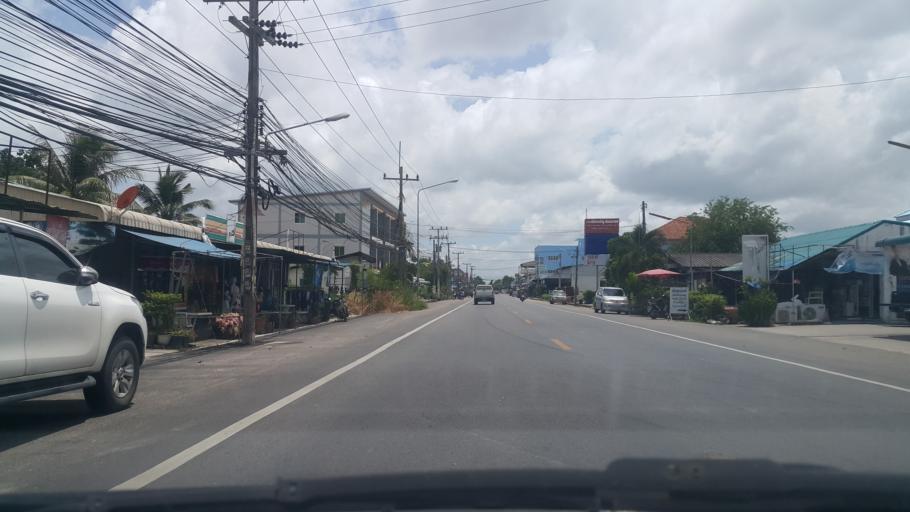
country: TH
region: Rayong
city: Ban Chang
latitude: 12.7498
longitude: 101.0385
